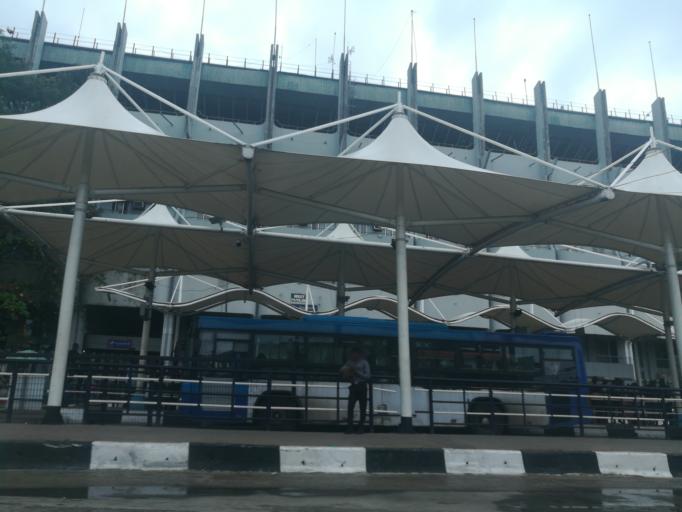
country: NG
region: Lagos
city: Lagos
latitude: 6.4457
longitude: 3.4008
